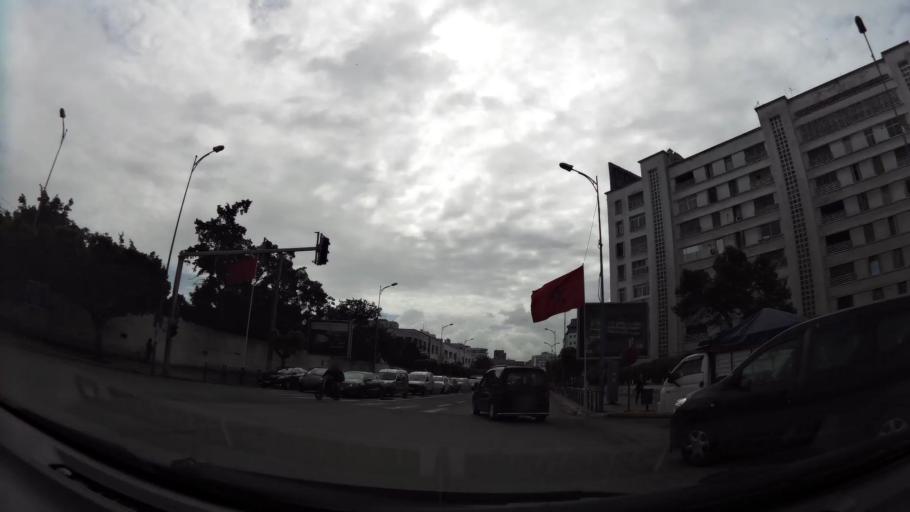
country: MA
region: Grand Casablanca
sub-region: Casablanca
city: Casablanca
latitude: 33.5853
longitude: -7.6287
